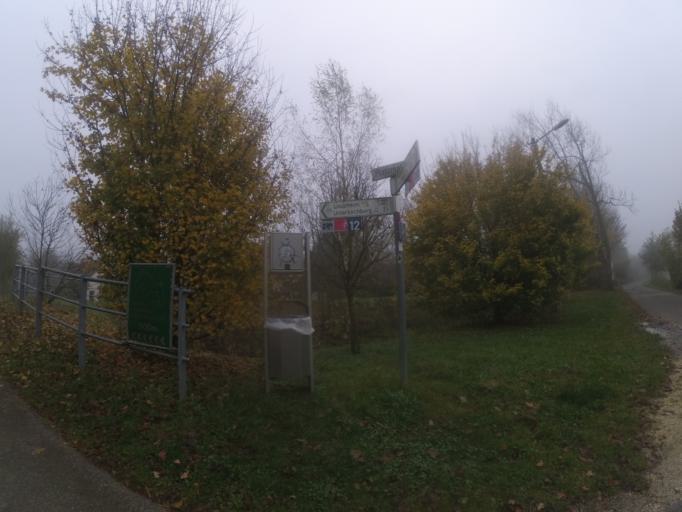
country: DE
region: Bavaria
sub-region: Swabia
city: Neu-Ulm
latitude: 48.3597
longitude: 9.9932
